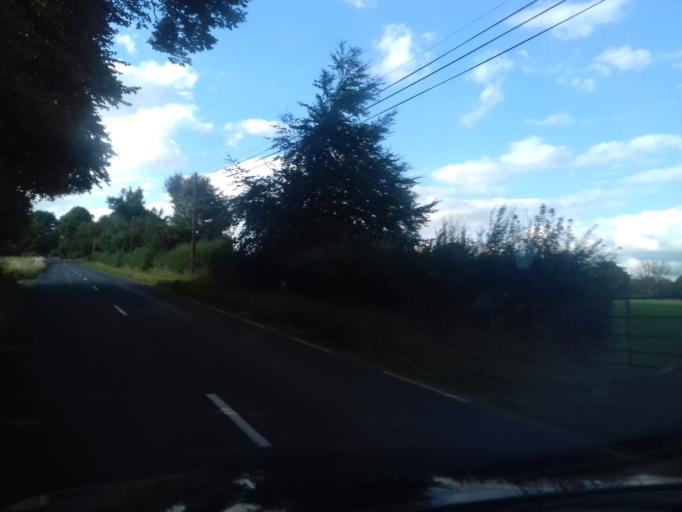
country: IE
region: Leinster
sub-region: Loch Garman
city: New Ross
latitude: 52.4421
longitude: -6.9608
